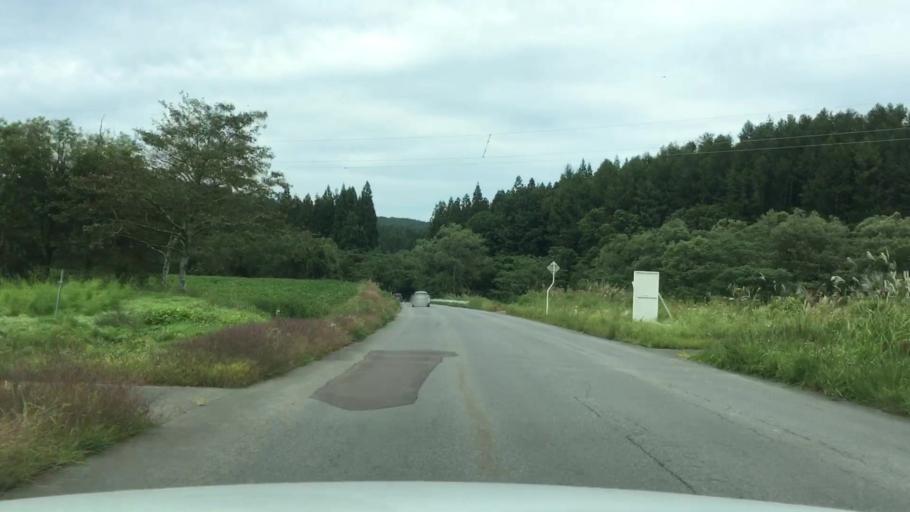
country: JP
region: Aomori
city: Shimokizukuri
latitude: 40.7136
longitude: 140.2643
